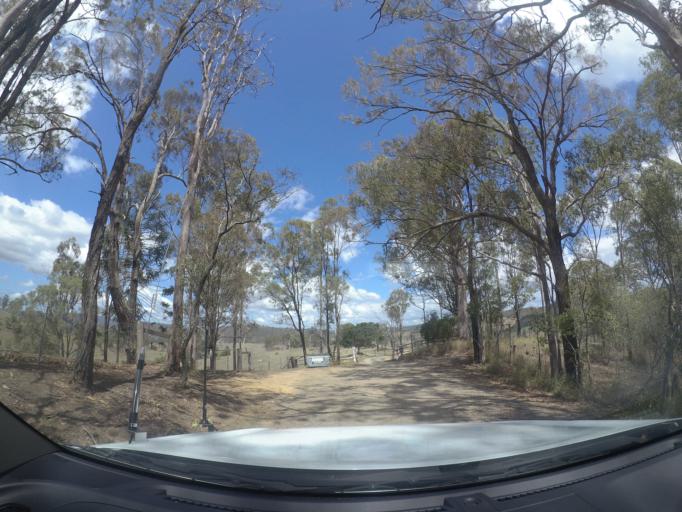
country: AU
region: Queensland
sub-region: Logan
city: Cedar Vale
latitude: -27.9008
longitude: 153.0460
